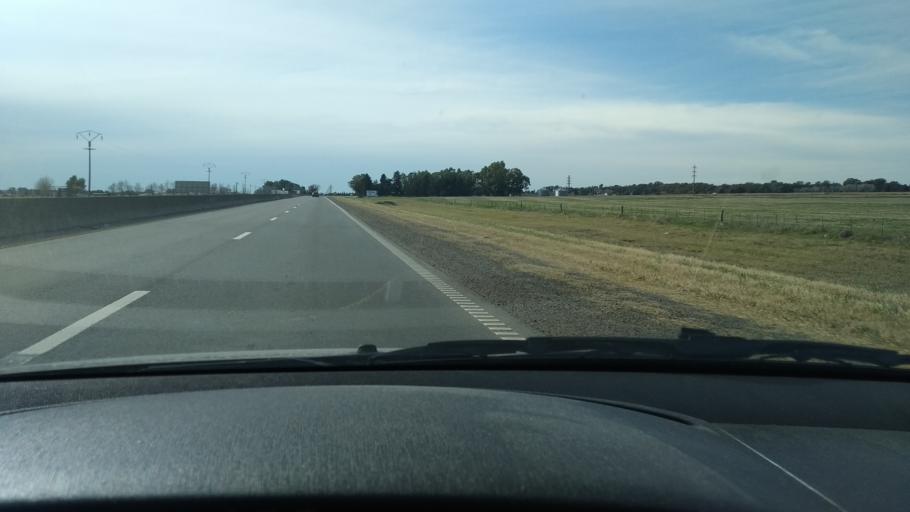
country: AR
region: Buenos Aires
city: Olavarria
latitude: -36.9076
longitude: -60.1933
